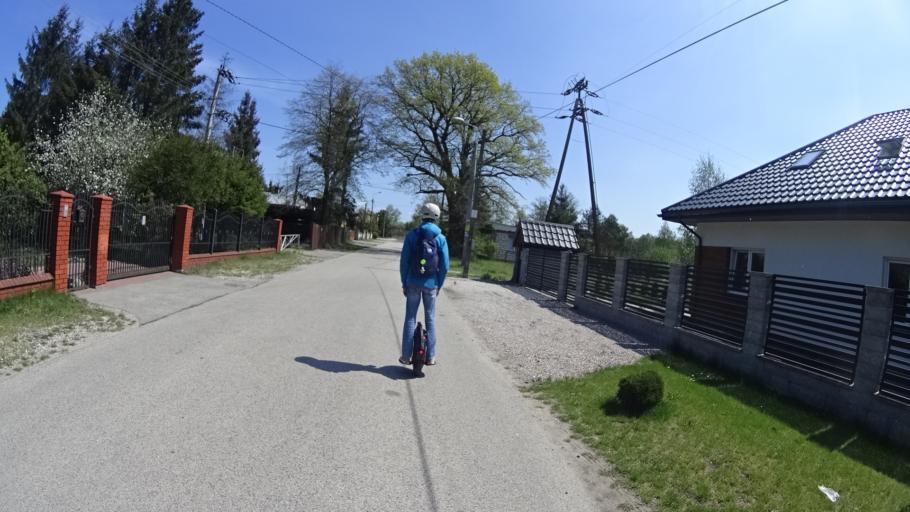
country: PL
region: Masovian Voivodeship
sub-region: Powiat warszawski zachodni
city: Truskaw
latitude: 52.2842
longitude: 20.7282
